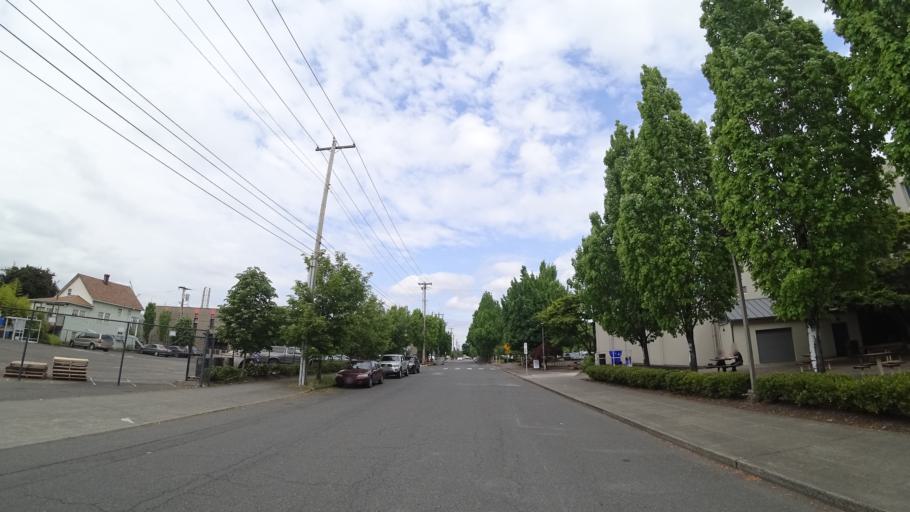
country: US
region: Oregon
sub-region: Multnomah County
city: Portland
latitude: 45.4951
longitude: -122.6435
